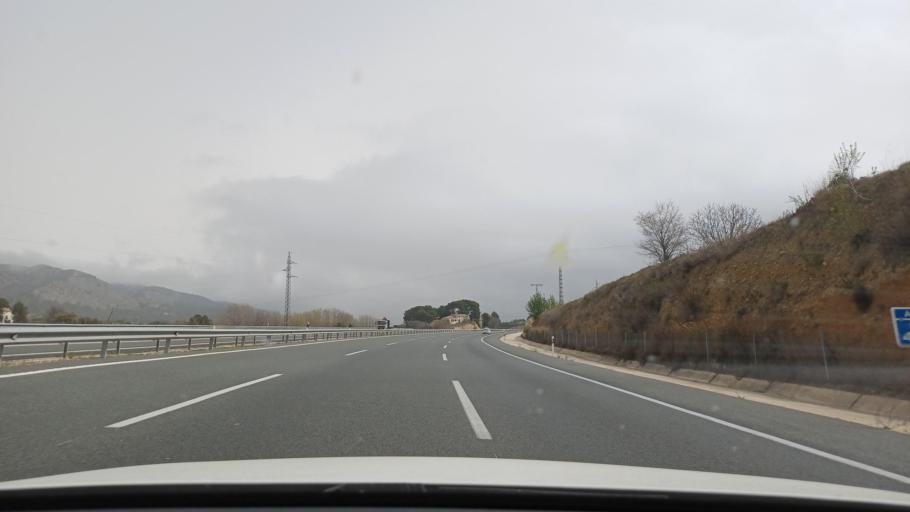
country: ES
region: Valencia
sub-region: Provincia de Alicante
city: Ibi
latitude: 38.6158
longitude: -0.5652
